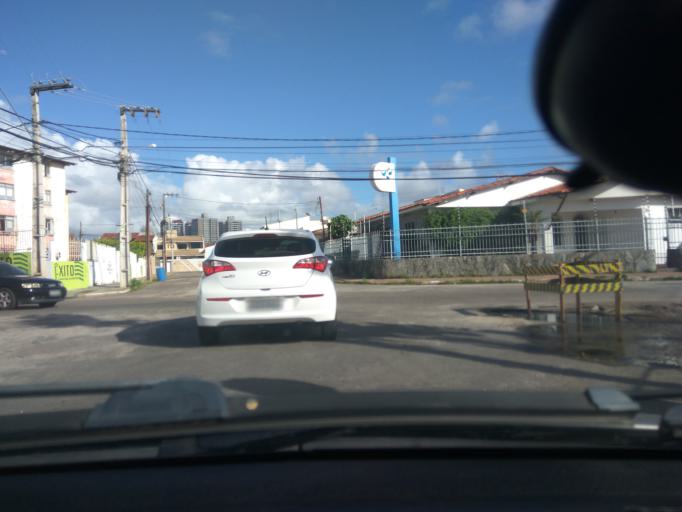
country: BR
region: Sergipe
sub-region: Aracaju
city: Aracaju
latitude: -10.9452
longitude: -37.0640
